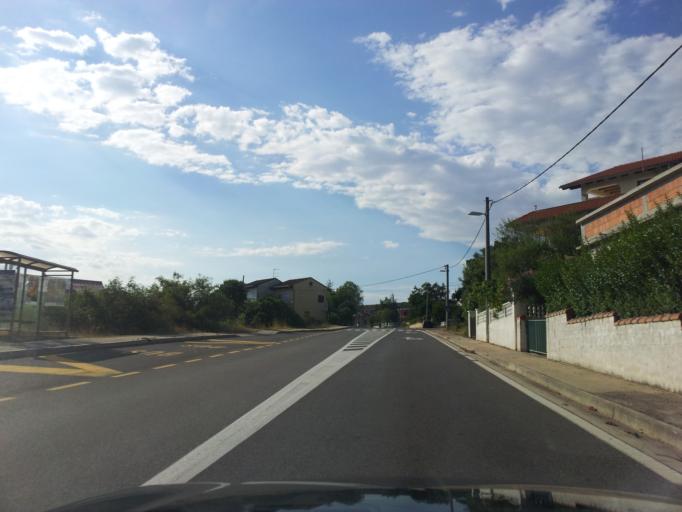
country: HR
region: Zadarska
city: Posedarje
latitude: 44.2152
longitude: 15.4683
